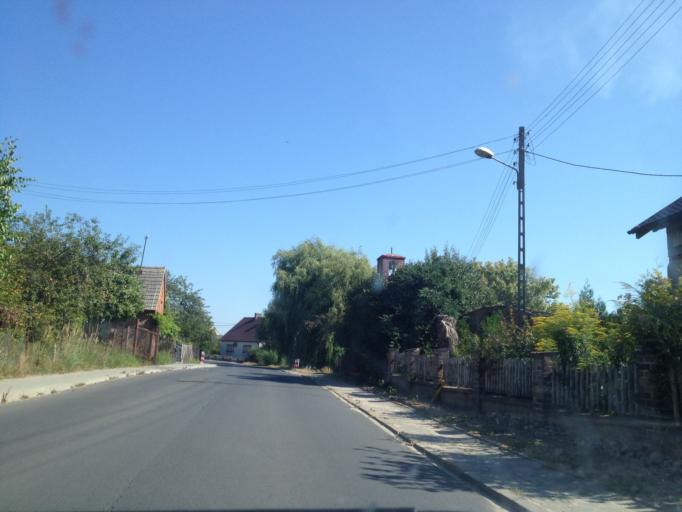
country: PL
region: Greater Poland Voivodeship
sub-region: Powiat sredzki
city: Zaniemysl
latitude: 52.1156
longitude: 17.1162
